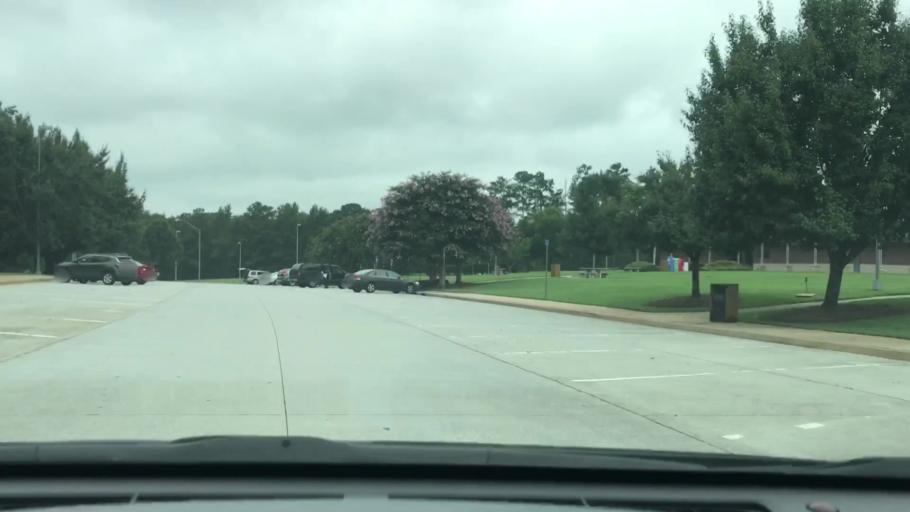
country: US
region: Georgia
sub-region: Morgan County
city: Madison
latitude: 33.5795
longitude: -83.5767
